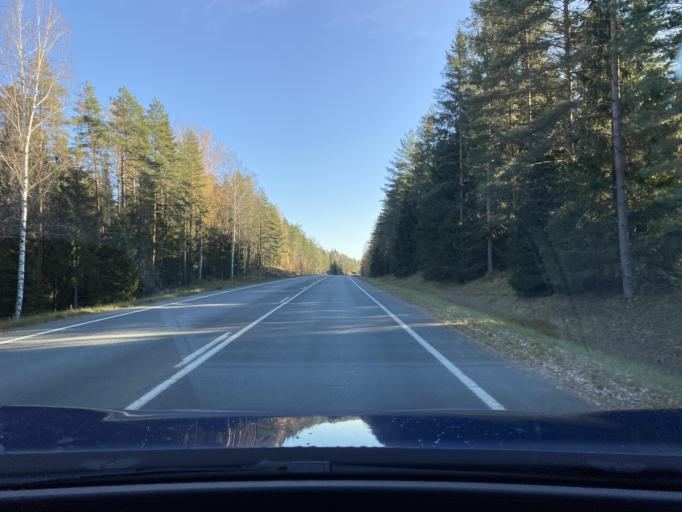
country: FI
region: Haeme
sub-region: Haemeenlinna
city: Parola
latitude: 61.0156
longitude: 24.3655
